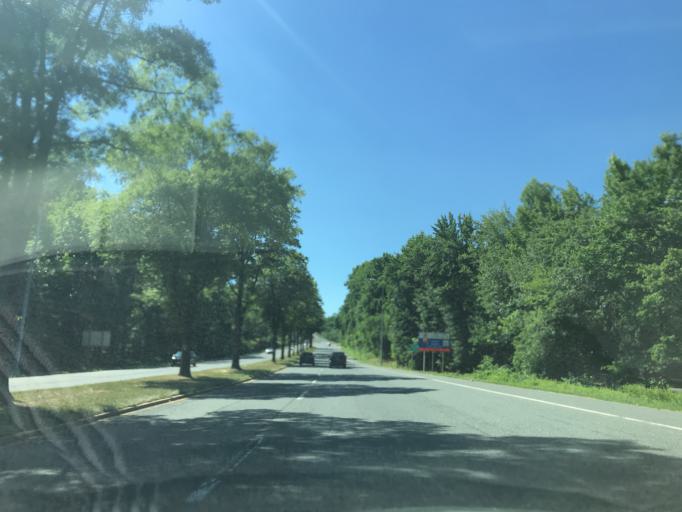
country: US
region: Maryland
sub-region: Harford County
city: Aberdeen
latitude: 39.5172
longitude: -76.1603
